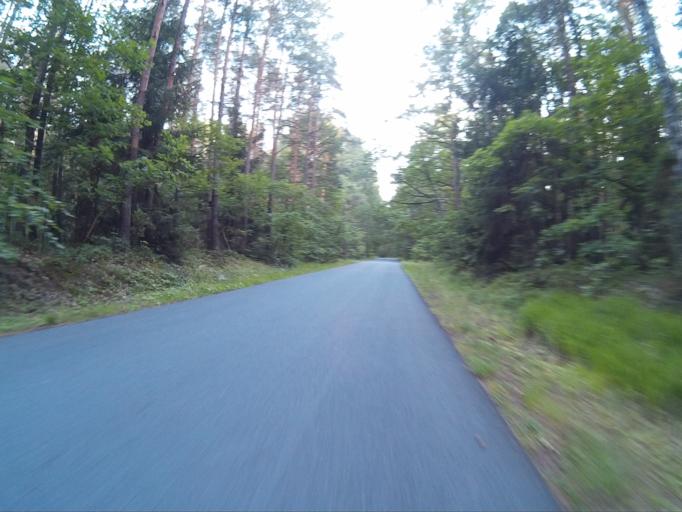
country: PL
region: Kujawsko-Pomorskie
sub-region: Powiat swiecki
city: Lniano
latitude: 53.5485
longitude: 18.1184
